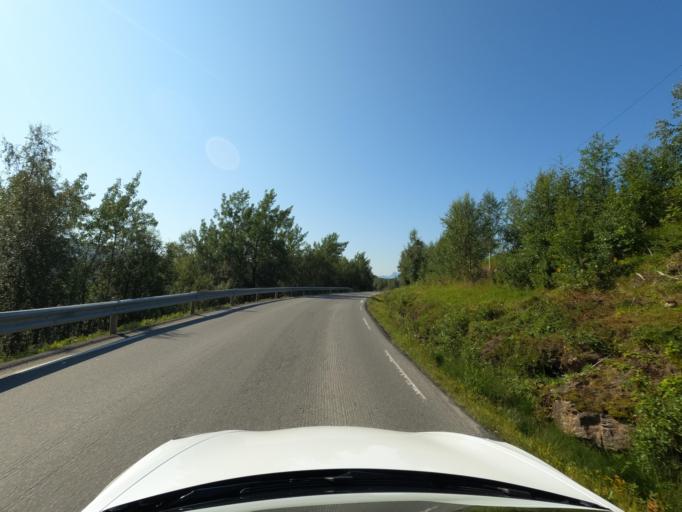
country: NO
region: Nordland
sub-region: Ballangen
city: Ballangen
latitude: 68.3578
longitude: 16.8736
